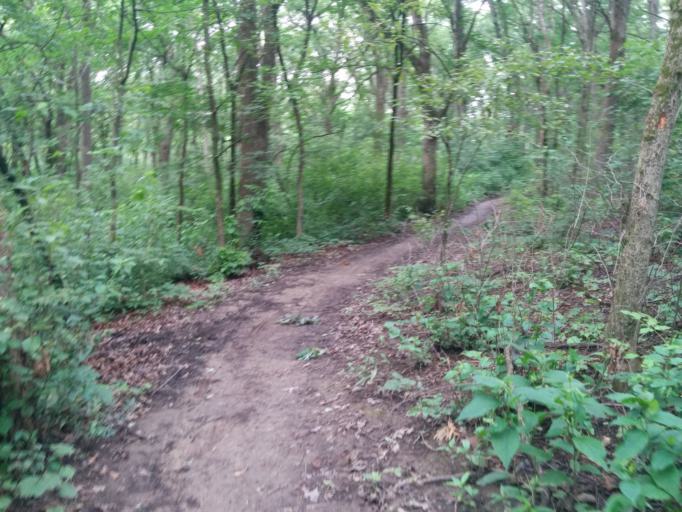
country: US
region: Illinois
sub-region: Cook County
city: Willow Springs
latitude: 41.7108
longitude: -87.8924
